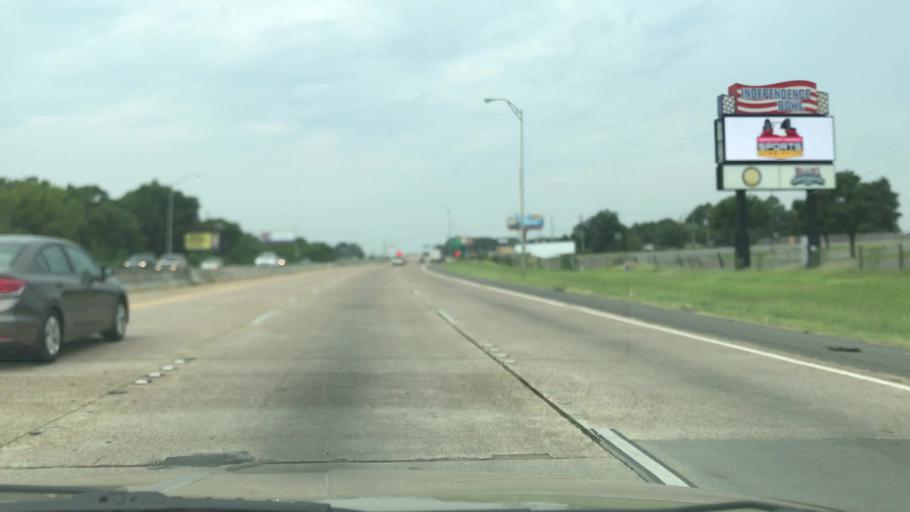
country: US
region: Louisiana
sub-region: Caddo Parish
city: Shreveport
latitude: 32.4739
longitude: -93.7914
